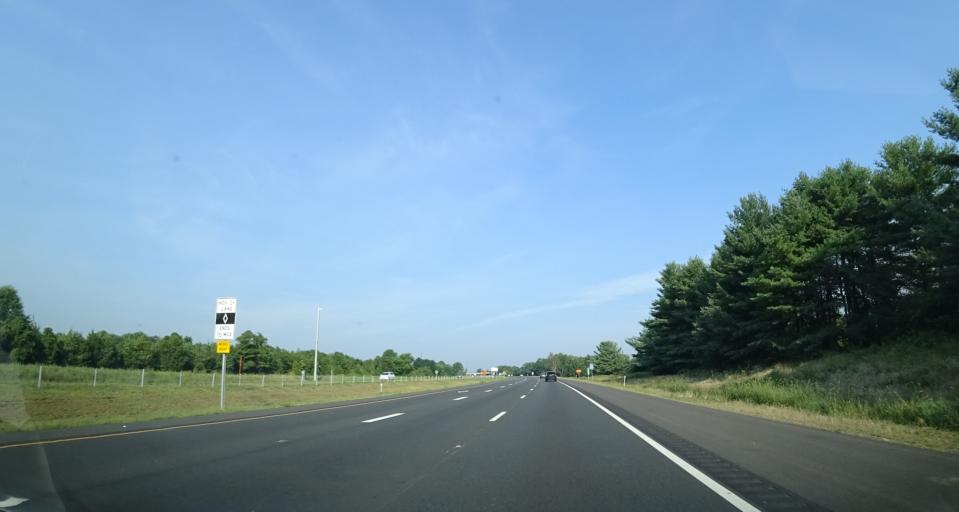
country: US
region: Virginia
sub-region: Prince William County
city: Haymarket
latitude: 38.8207
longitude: -77.6472
